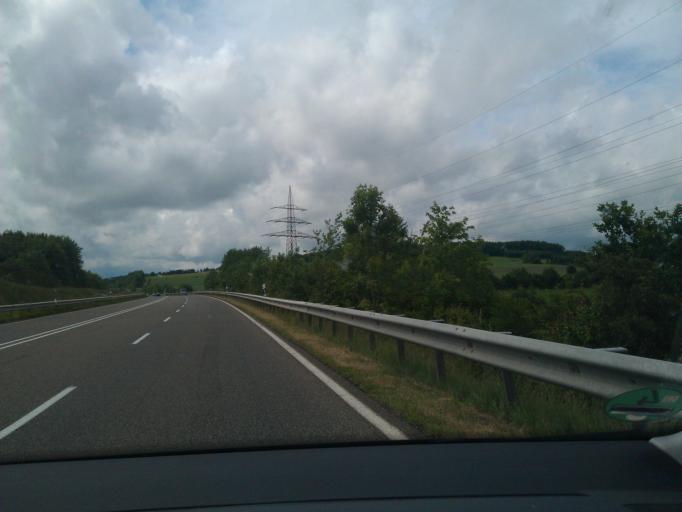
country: DE
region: Rheinland-Pfalz
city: Watzerath
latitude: 50.1976
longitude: 6.3707
